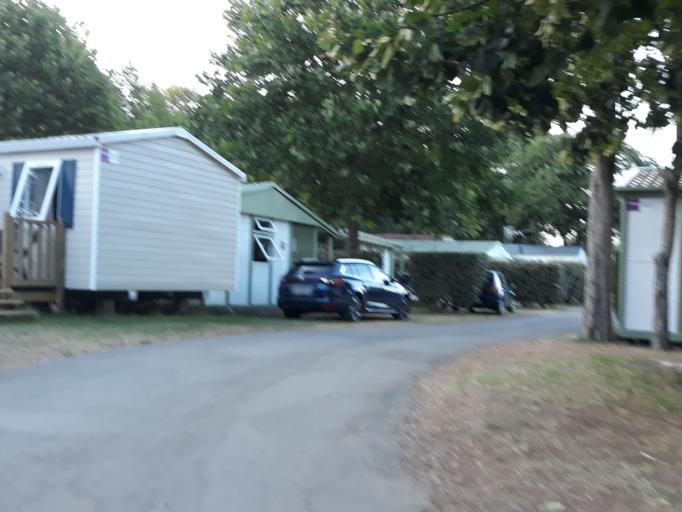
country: FR
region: Poitou-Charentes
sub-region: Departement de la Charente-Maritime
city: Saint-Laurent-de-la-Pree
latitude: 45.9881
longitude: -1.0525
